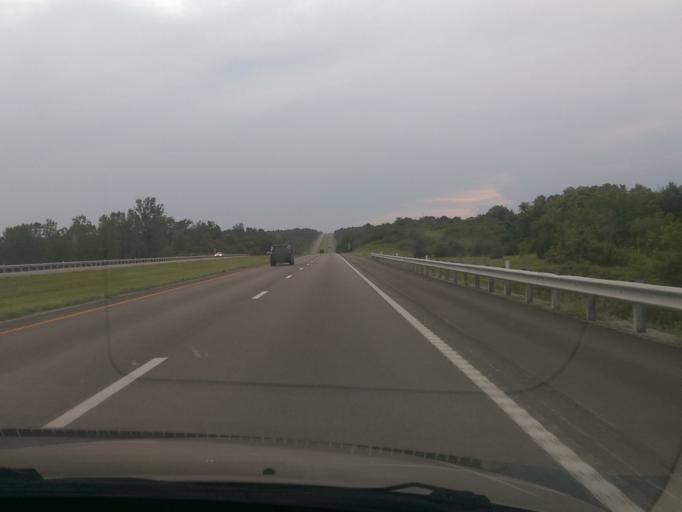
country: US
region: Missouri
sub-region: Andrew County
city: Savannah
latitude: 39.9317
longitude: -94.9249
